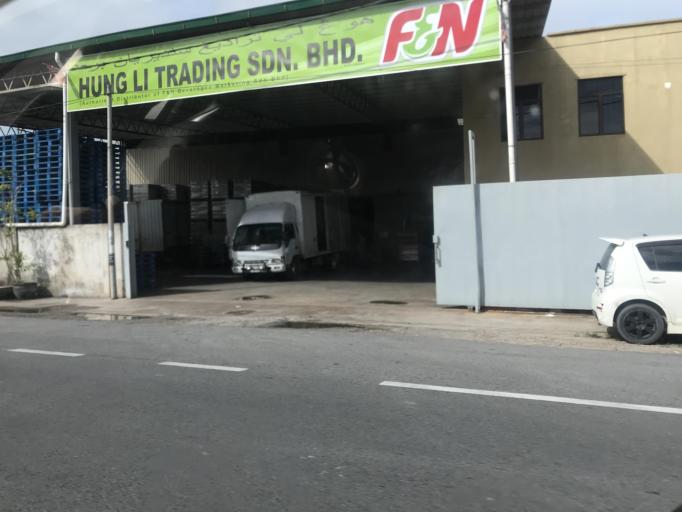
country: MY
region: Kelantan
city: Kota Bharu
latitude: 6.1226
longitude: 102.1853
